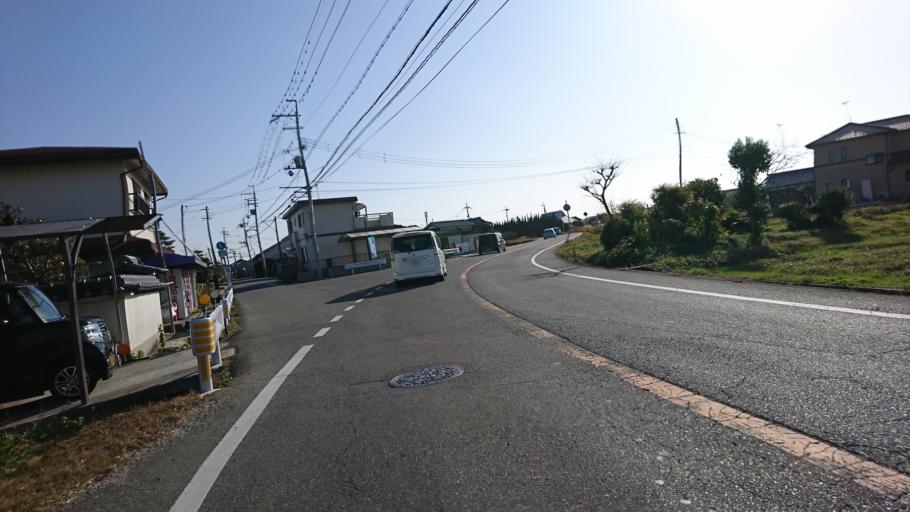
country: JP
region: Hyogo
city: Kakogawacho-honmachi
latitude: 34.7627
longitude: 134.9096
